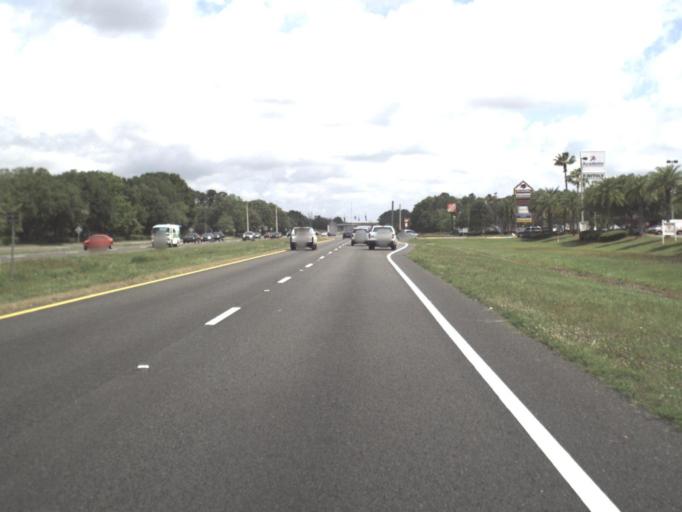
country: US
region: Florida
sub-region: Saint Johns County
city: Fruit Cove
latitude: 30.1919
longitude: -81.5516
